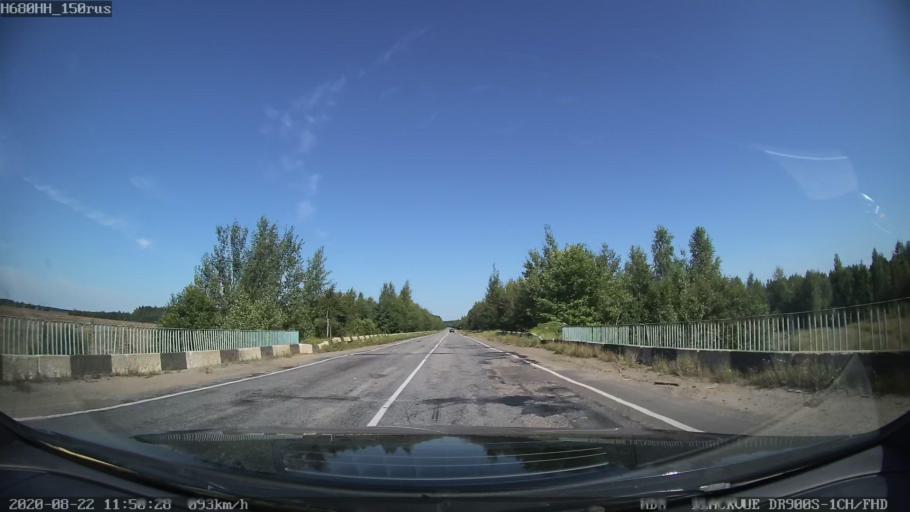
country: RU
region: Tverskaya
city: Sakharovo
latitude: 57.0906
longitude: 36.1164
